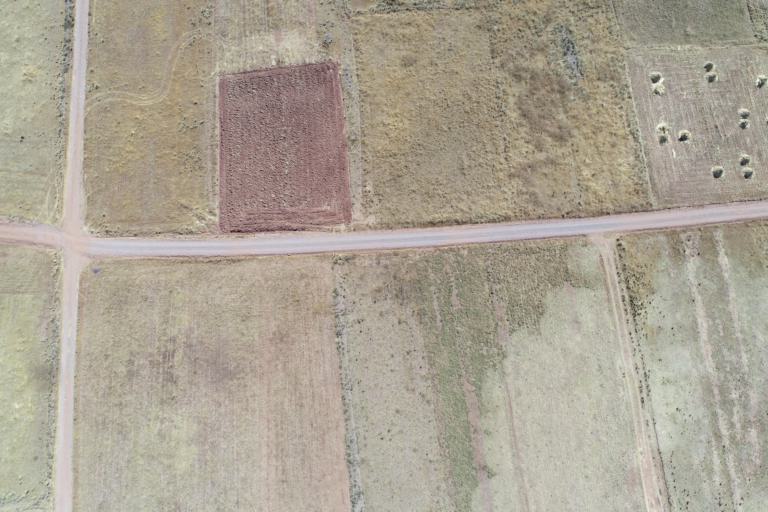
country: BO
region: La Paz
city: Tiahuanaco
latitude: -16.5947
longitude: -68.7813
